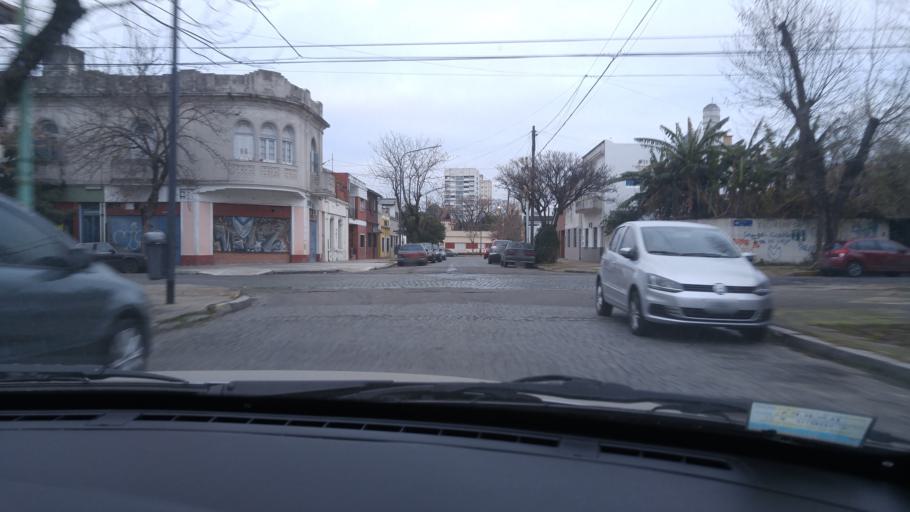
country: AR
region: Buenos Aires F.D.
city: Villa Santa Rita
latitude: -34.6329
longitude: -58.5243
